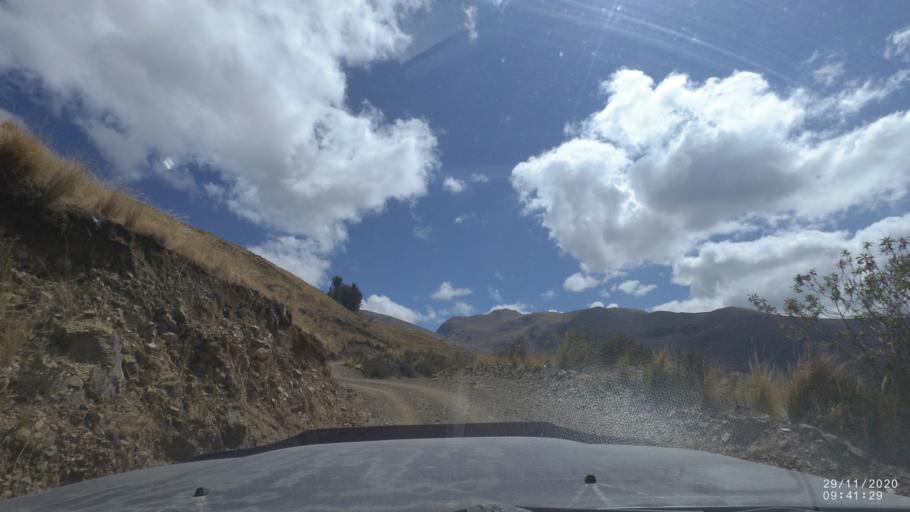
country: BO
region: Cochabamba
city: Cochabamba
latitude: -17.3026
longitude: -66.1822
